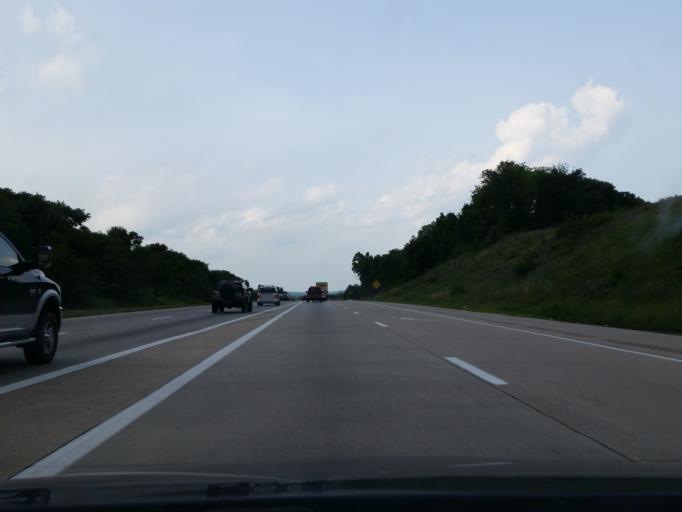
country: US
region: Pennsylvania
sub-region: Dauphin County
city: Colonial Park
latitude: 40.3132
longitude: -76.8292
